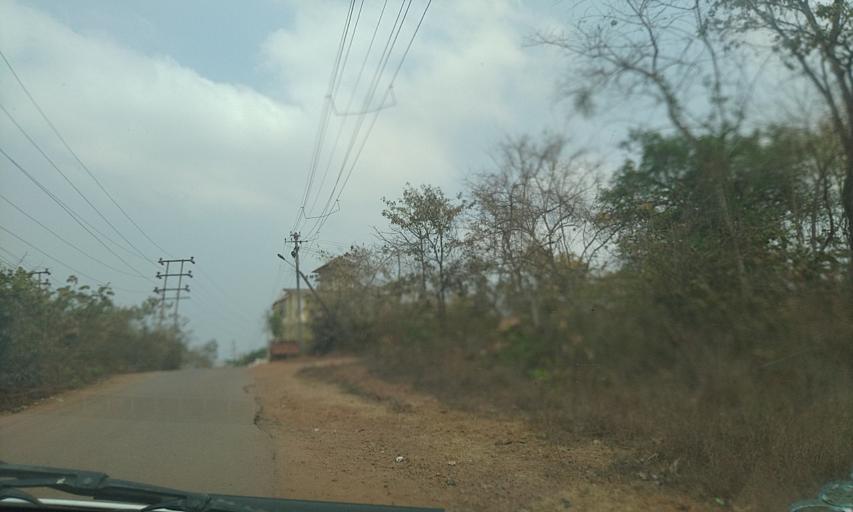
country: IN
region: Goa
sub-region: North Goa
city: Serula
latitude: 15.5379
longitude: 73.8268
